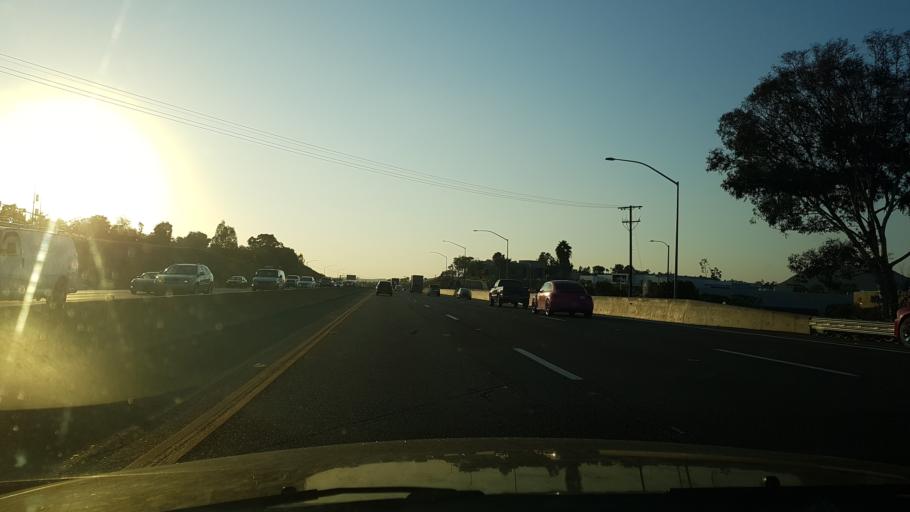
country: US
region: California
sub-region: San Diego County
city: San Marcos
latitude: 33.1395
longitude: -117.1438
